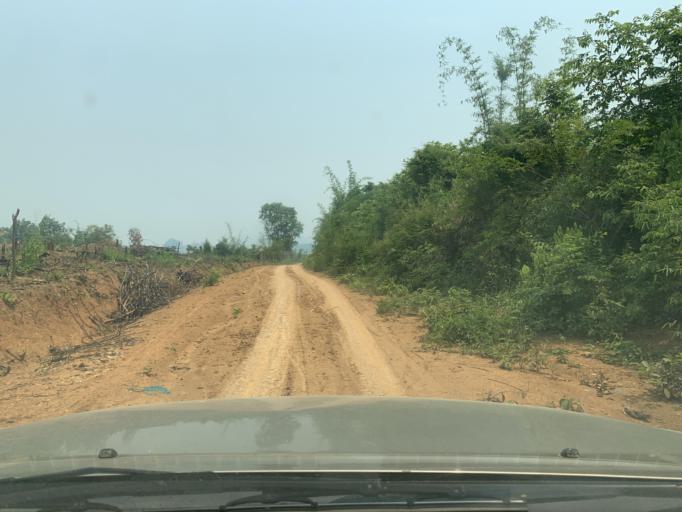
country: LA
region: Louangphabang
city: Xiang Ngeun
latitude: 19.8361
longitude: 102.2265
